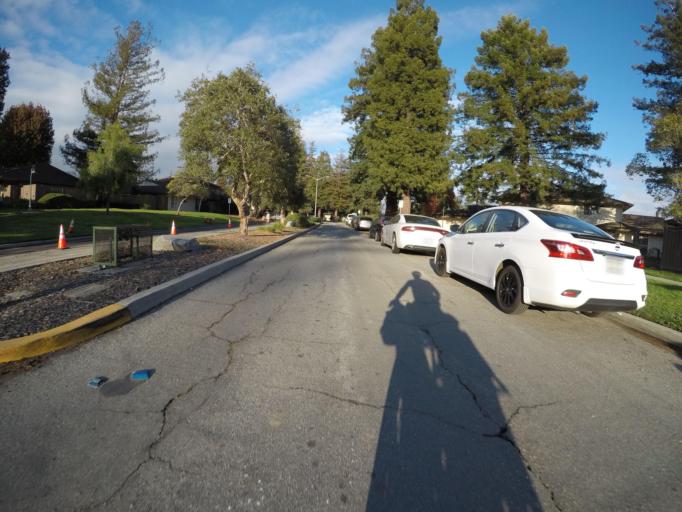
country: US
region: California
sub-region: Santa Cruz County
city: Santa Cruz
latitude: 36.9712
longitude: -122.0506
